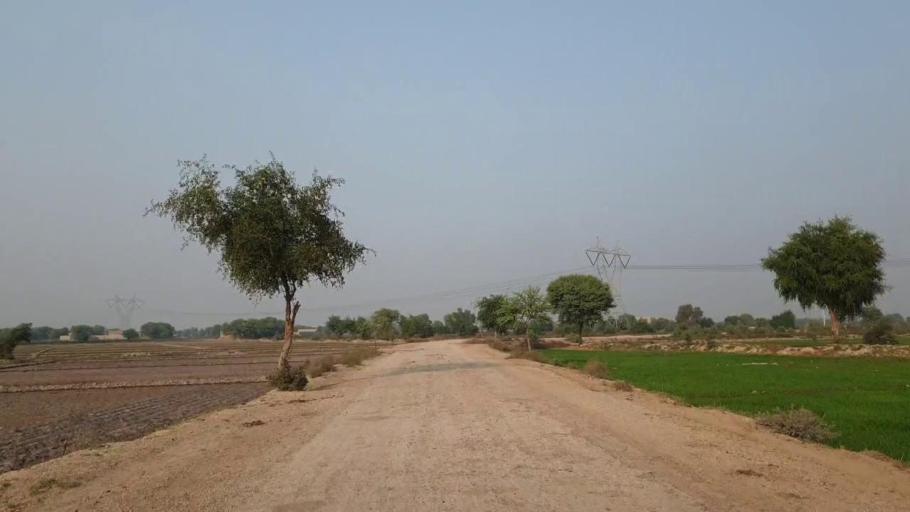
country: PK
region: Sindh
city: Bhan
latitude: 26.4993
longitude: 67.7511
